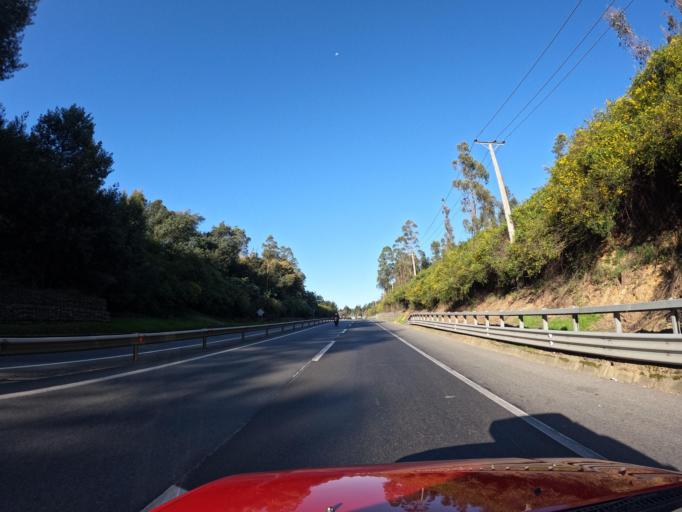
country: CL
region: Biobio
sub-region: Provincia de Concepcion
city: Penco
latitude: -36.7608
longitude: -72.9724
